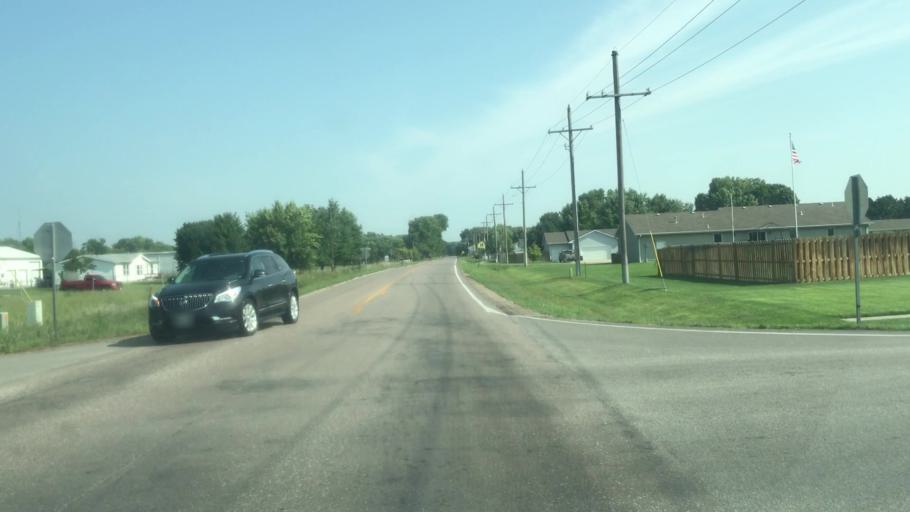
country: US
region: Nebraska
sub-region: Hall County
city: Grand Island
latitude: 40.9158
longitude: -98.3018
